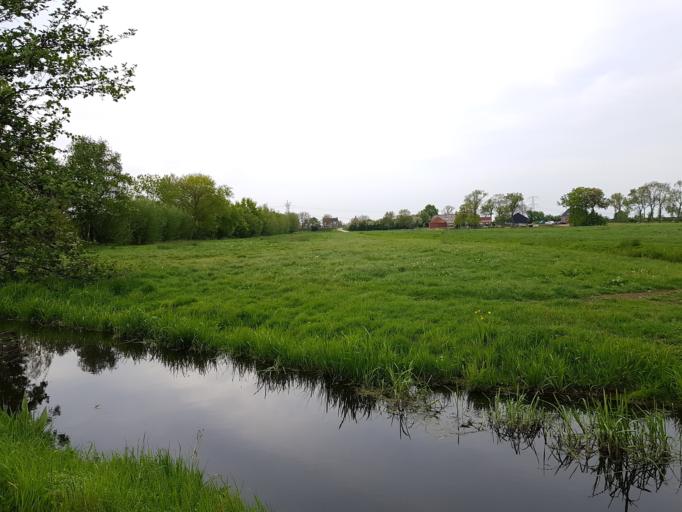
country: NL
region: South Holland
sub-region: Gemeente Vlist
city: Haastrecht
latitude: 51.9974
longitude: 4.7591
